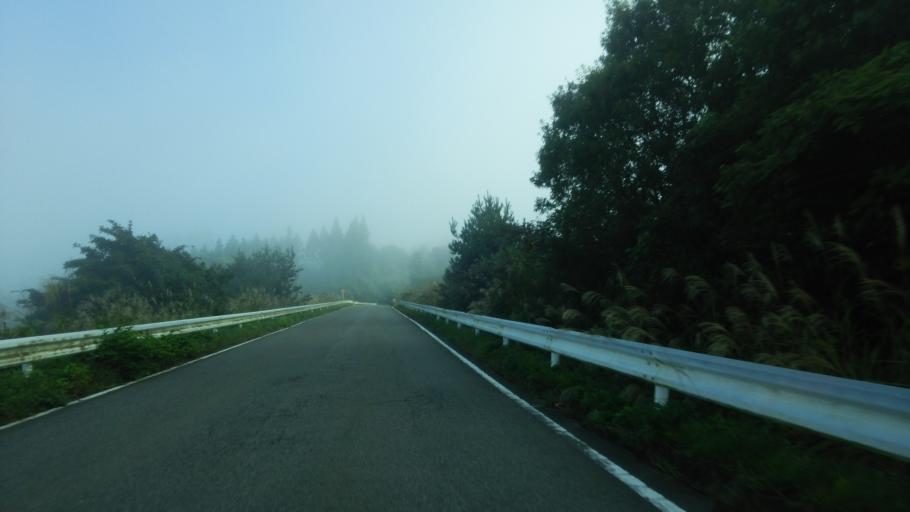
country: JP
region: Fukushima
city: Kitakata
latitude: 37.5986
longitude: 139.7792
